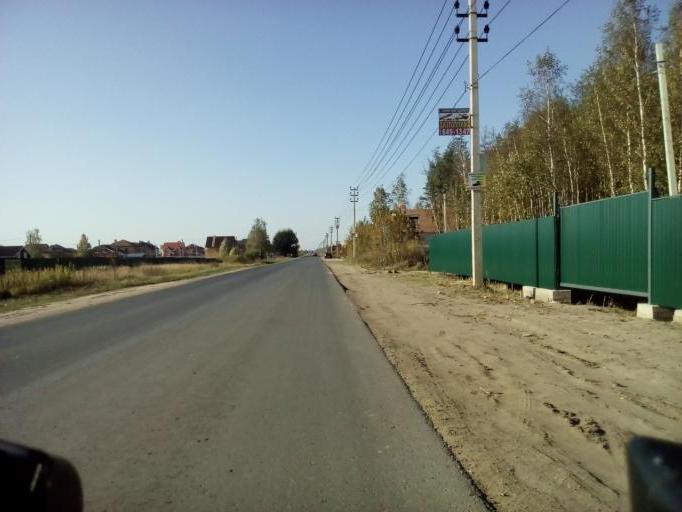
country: RU
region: Moskovskaya
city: Ramenskoye
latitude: 55.5626
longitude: 38.3045
